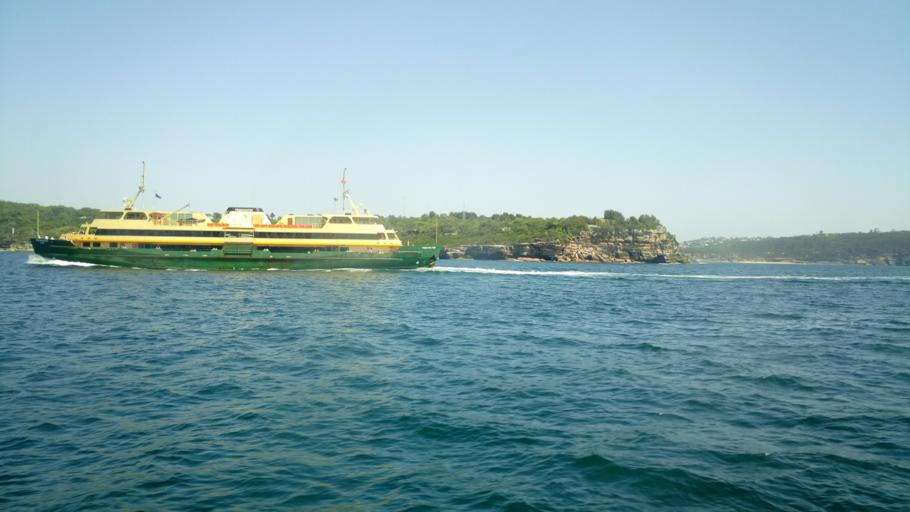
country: AU
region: New South Wales
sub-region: Manly Vale
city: Clontarf
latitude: -33.8314
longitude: 151.2720
